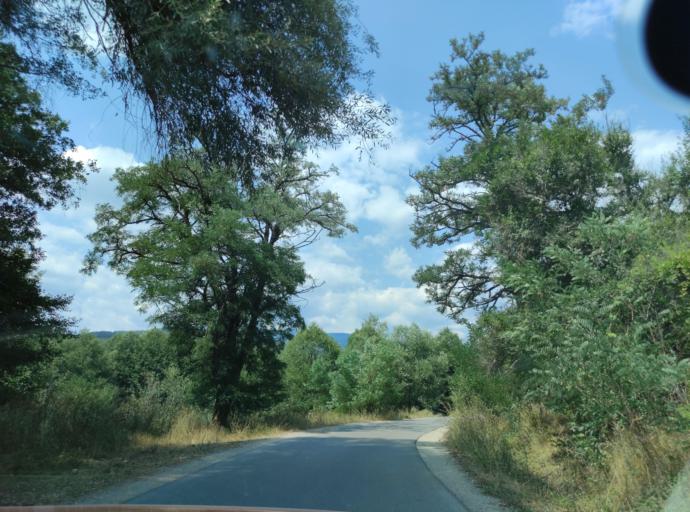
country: BG
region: Blagoevgrad
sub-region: Obshtina Belitsa
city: Belitsa
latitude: 41.9762
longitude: 23.5539
